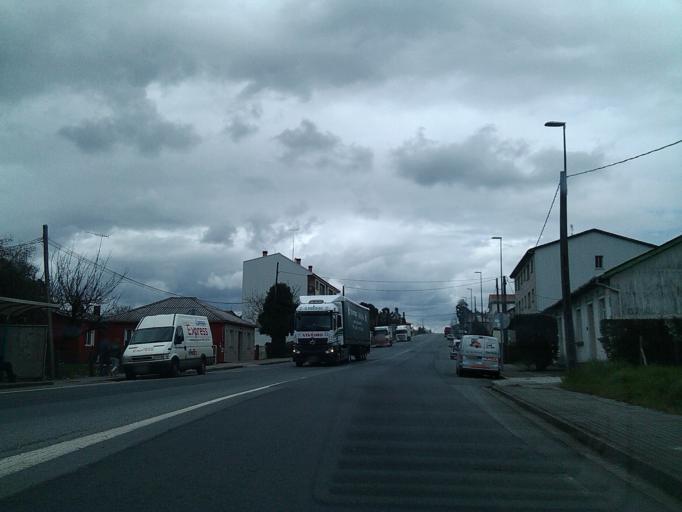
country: ES
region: Galicia
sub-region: Provincia da Coruna
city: Curtis
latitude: 43.1349
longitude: -8.0341
